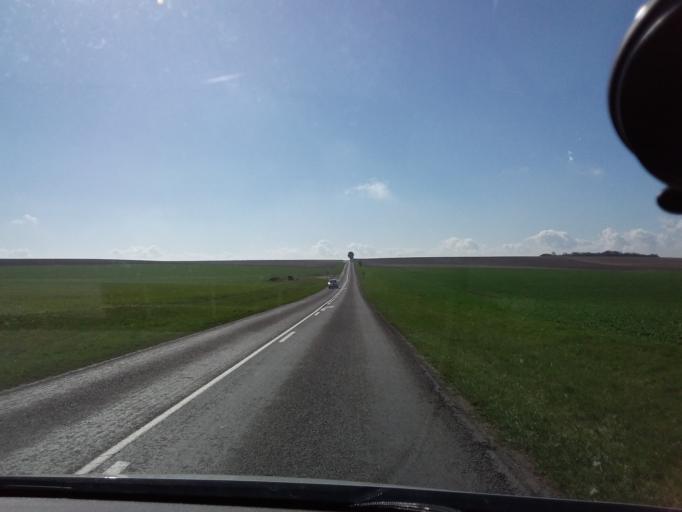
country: FR
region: Picardie
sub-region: Departement de l'Aisne
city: Guignicourt
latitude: 49.5157
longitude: 4.0420
